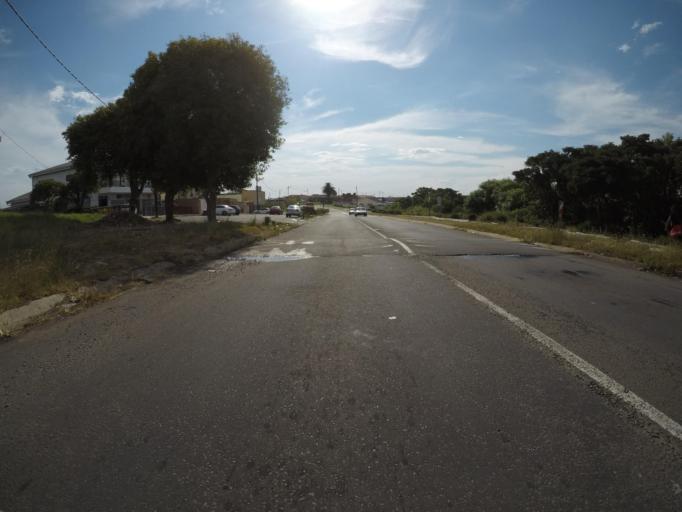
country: ZA
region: Eastern Cape
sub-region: Buffalo City Metropolitan Municipality
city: East London
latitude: -33.0221
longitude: 27.8711
